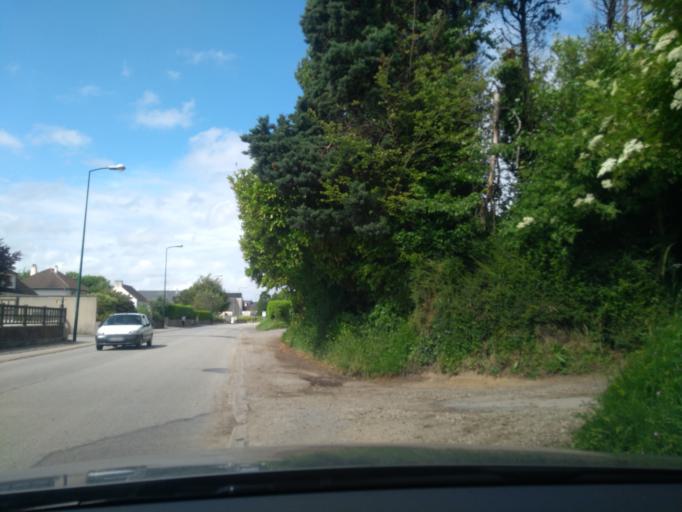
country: FR
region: Lower Normandy
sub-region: Departement de la Manche
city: Quettehou
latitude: 49.5890
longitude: -1.3024
